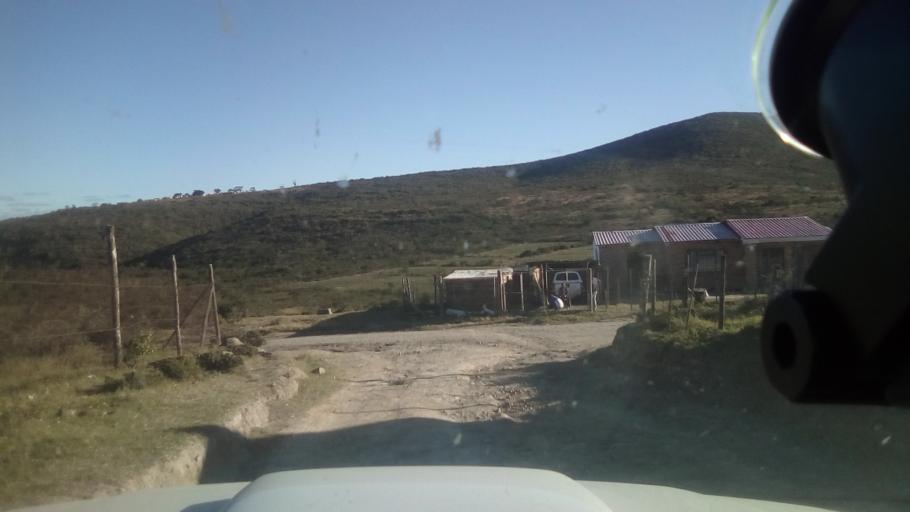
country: ZA
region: Eastern Cape
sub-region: Buffalo City Metropolitan Municipality
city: Bhisho
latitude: -32.7345
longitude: 27.3602
